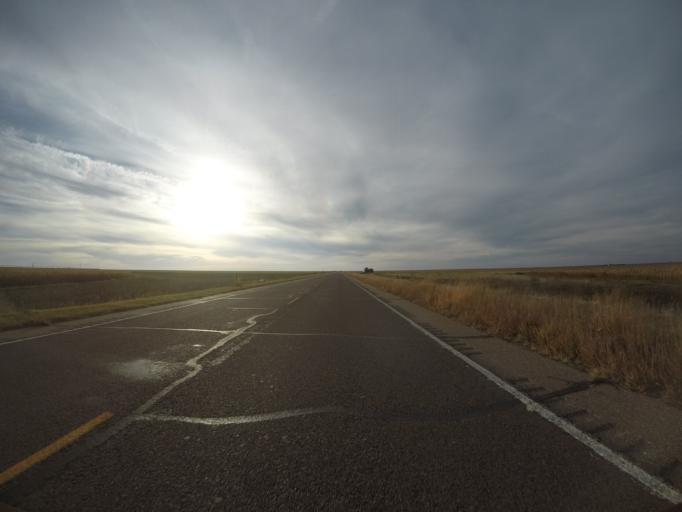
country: US
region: Colorado
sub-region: Kit Carson County
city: Burlington
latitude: 39.6578
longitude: -102.4766
